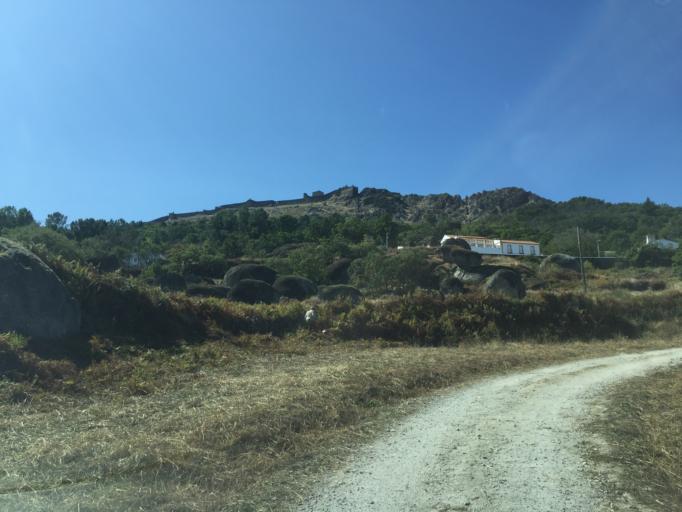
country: PT
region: Portalegre
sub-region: Marvao
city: Marvao
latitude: 39.4024
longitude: -7.3750
